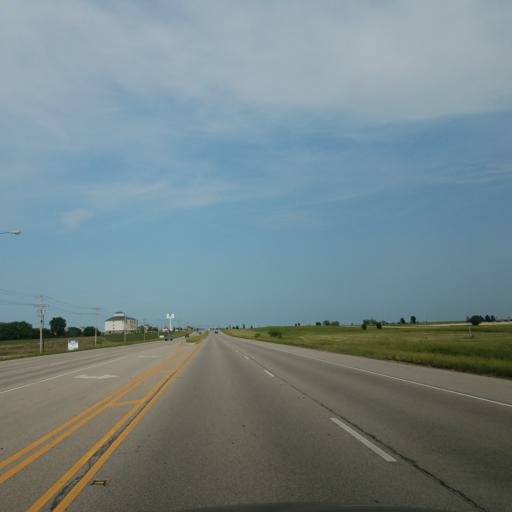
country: US
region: Illinois
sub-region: McLean County
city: Bloomington
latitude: 40.4882
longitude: -88.9185
